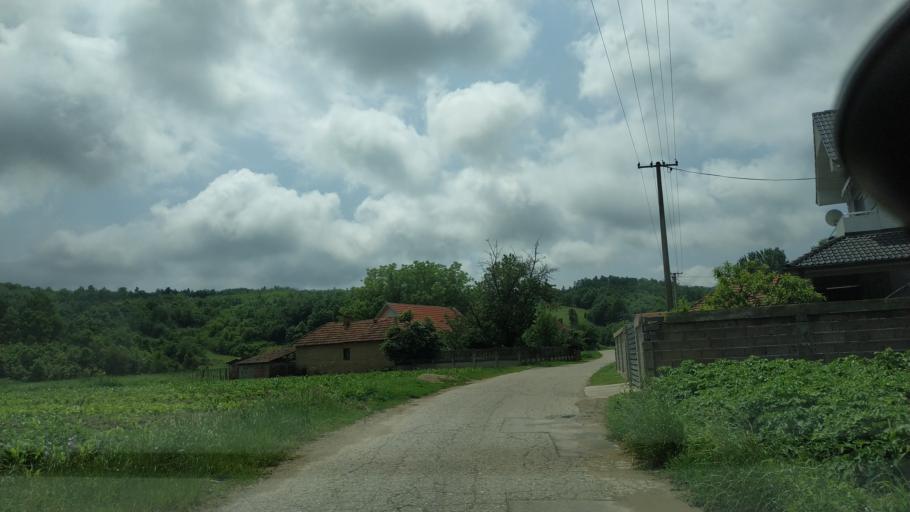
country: RS
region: Central Serbia
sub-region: Nisavski Okrug
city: Aleksinac
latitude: 43.4273
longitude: 21.7098
